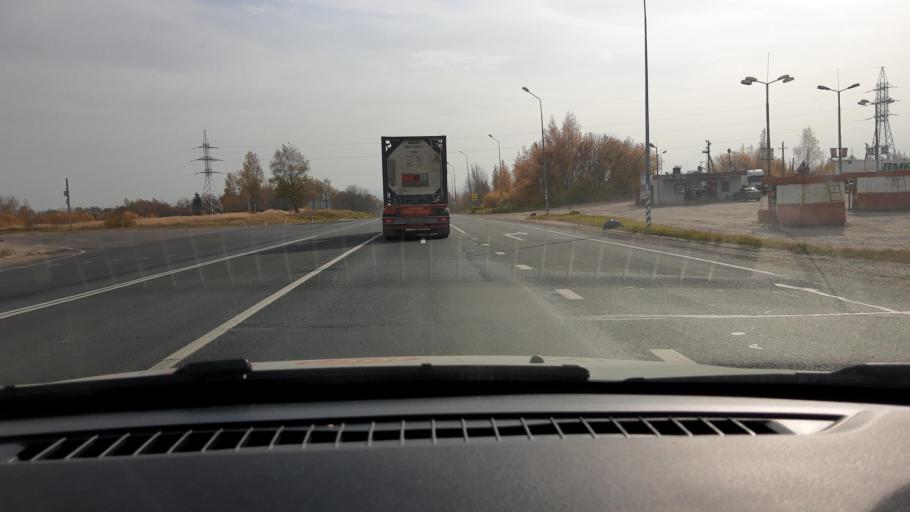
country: RU
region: Nizjnij Novgorod
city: Kstovo
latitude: 56.1105
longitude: 44.2838
